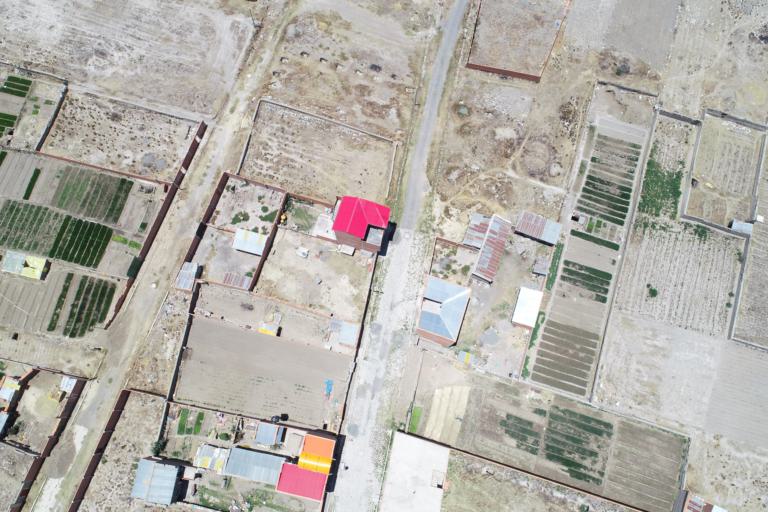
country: BO
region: La Paz
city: Achacachi
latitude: -16.0403
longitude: -68.6903
